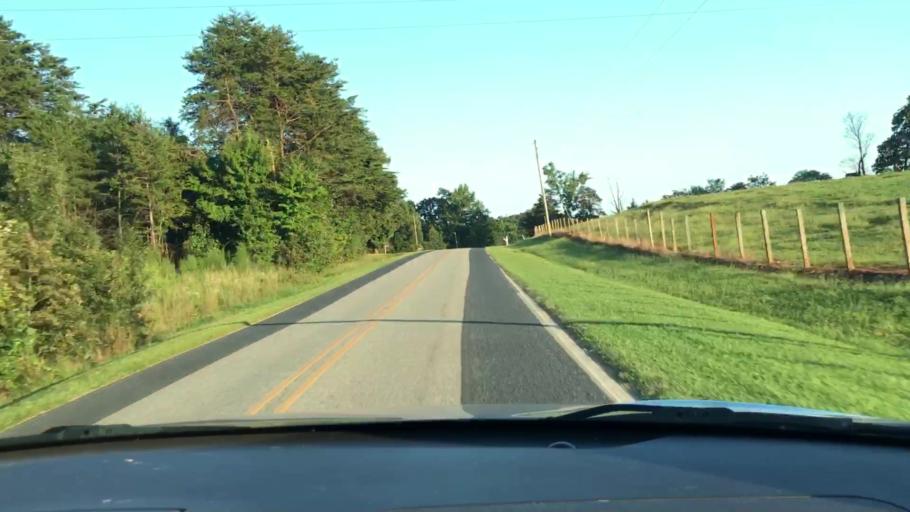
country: US
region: North Carolina
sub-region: Randolph County
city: Ramseur
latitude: 35.7781
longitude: -79.6328
